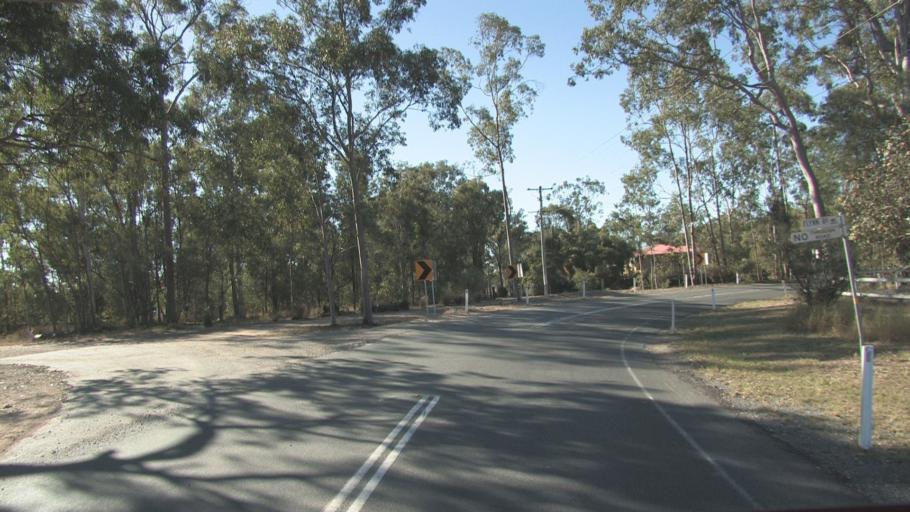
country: AU
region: Queensland
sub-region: Logan
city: North Maclean
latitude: -27.7902
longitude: 153.0277
